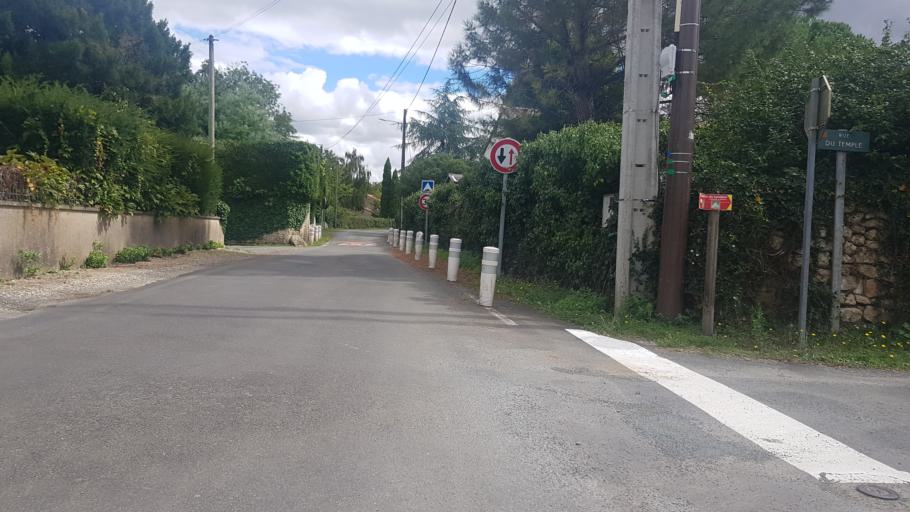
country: FR
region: Poitou-Charentes
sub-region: Departement des Deux-Sevres
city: Vouille
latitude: 46.3279
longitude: -0.3445
